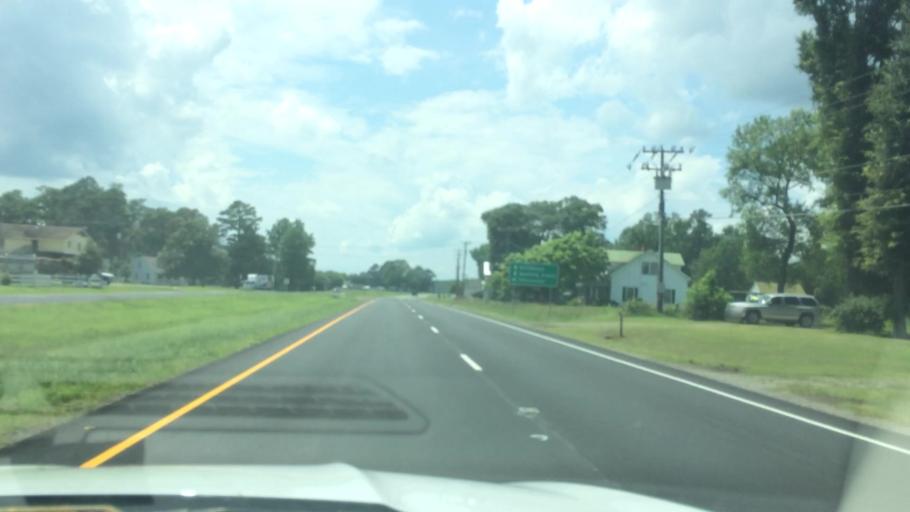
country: US
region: Virginia
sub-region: King William County
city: West Point
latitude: 37.5441
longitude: -76.7021
